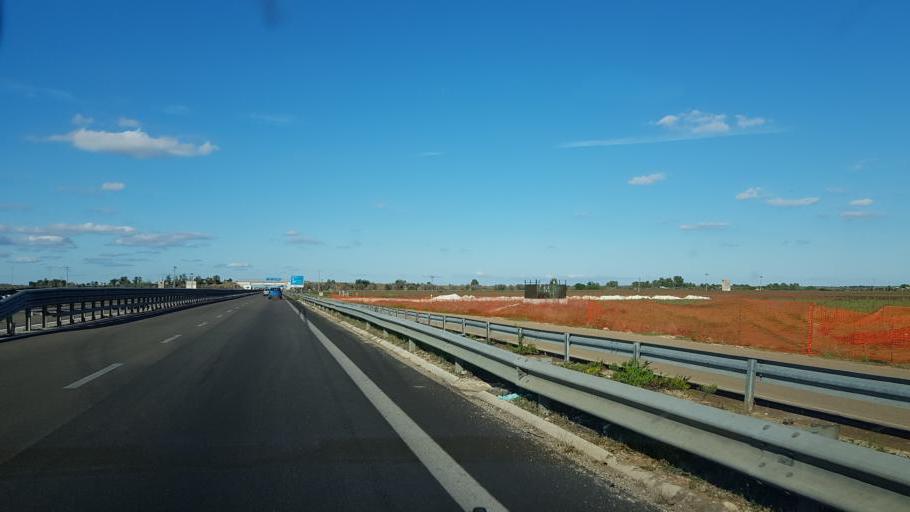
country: IT
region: Apulia
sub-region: Provincia di Lecce
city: Collemeto
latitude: 40.2522
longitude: 18.1164
